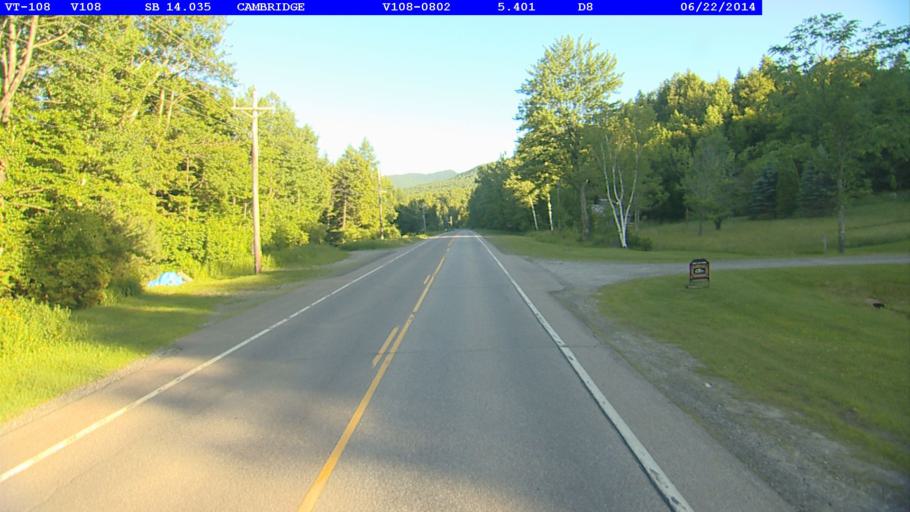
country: US
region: Vermont
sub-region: Lamoille County
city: Johnson
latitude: 44.6024
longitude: -72.8088
